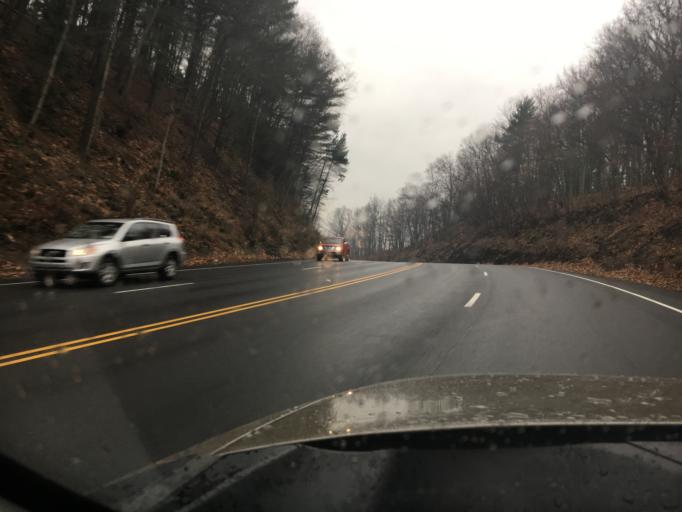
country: US
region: Pennsylvania
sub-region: Luzerne County
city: Harleigh
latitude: 41.0280
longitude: -75.9635
